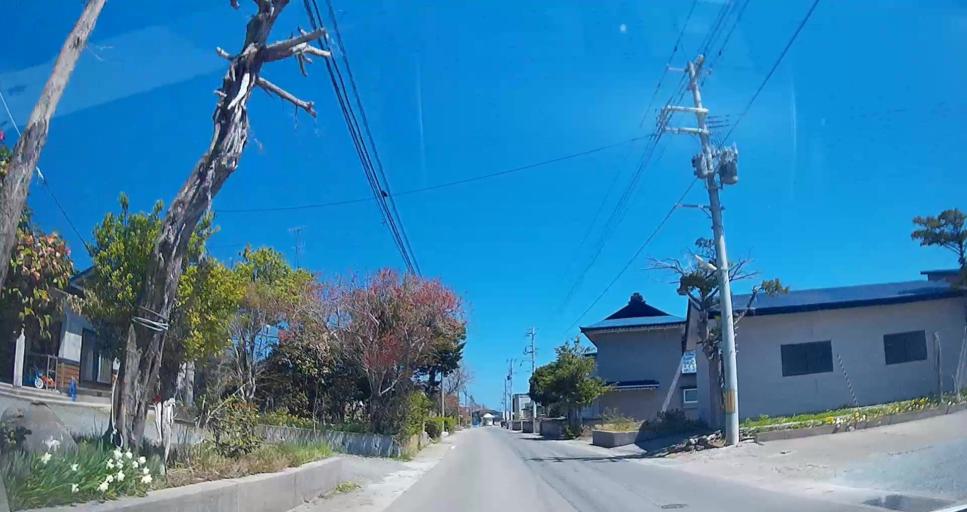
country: JP
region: Aomori
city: Mutsu
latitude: 41.2284
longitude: 141.3951
